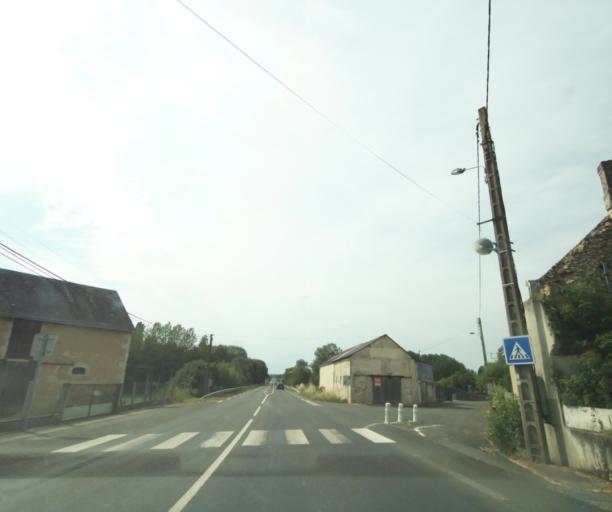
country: FR
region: Centre
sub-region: Departement d'Indre-et-Loire
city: Saint-Christophe-sur-le-Nais
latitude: 47.6628
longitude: 0.4754
